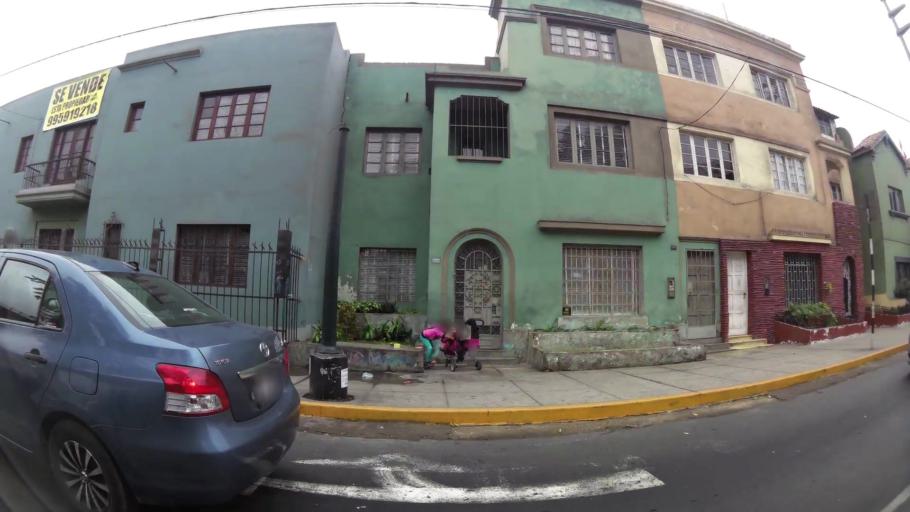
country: PE
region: Callao
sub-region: Callao
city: Callao
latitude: -12.0598
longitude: -77.1274
